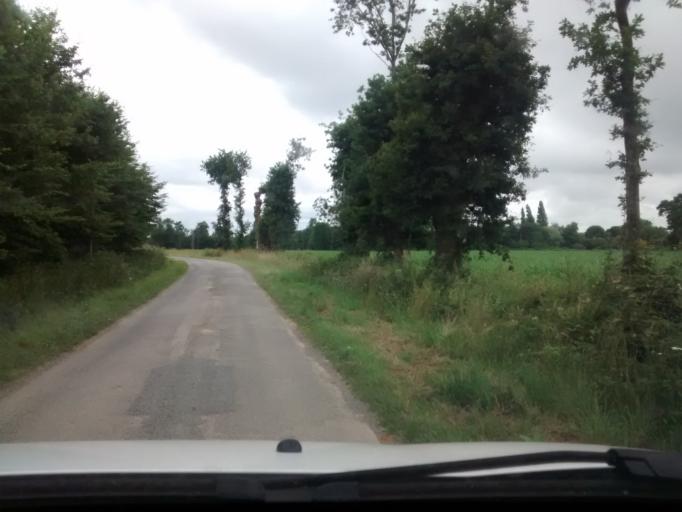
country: FR
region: Brittany
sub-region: Departement d'Ille-et-Vilaine
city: Saint-Gregoire
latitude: 48.1680
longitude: -1.6646
